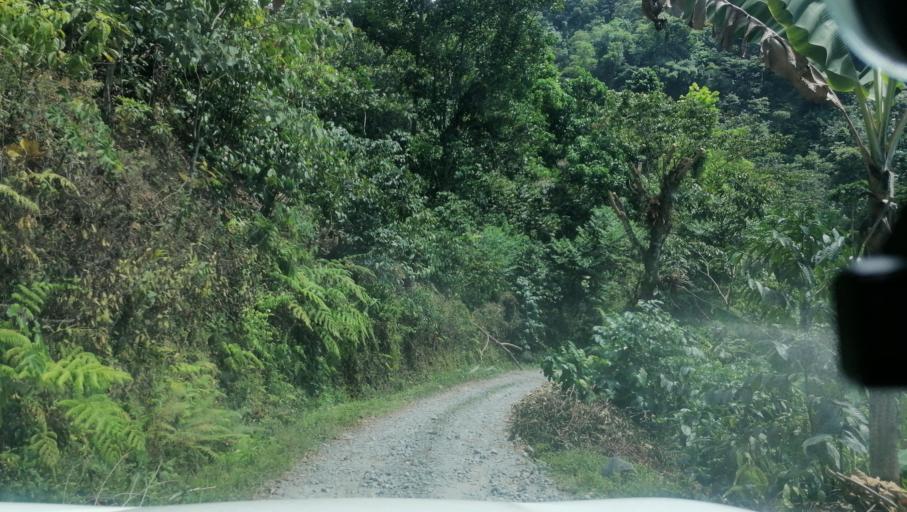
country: MX
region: Chiapas
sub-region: Union Juarez
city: Santo Domingo
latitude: 15.0726
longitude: -92.1312
